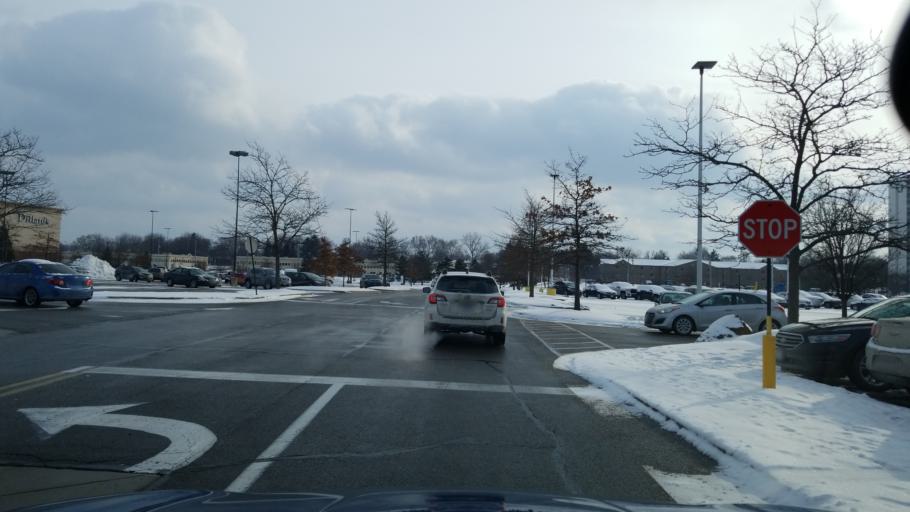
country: US
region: Ohio
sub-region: Cuyahoga County
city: North Olmsted
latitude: 41.4164
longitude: -81.9096
